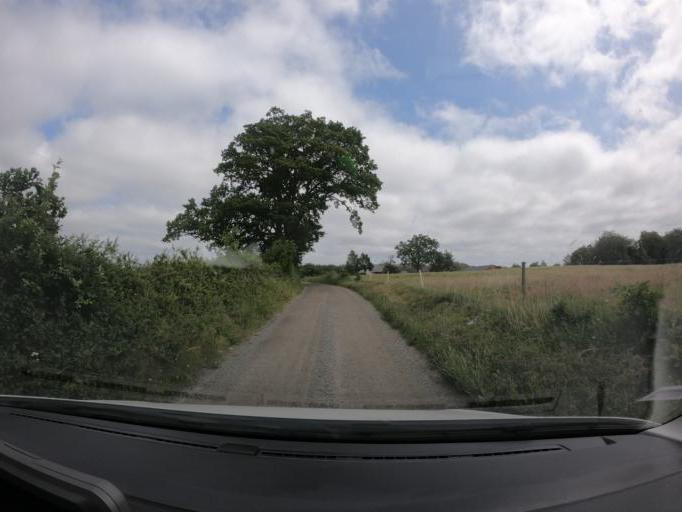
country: SE
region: Skane
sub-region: Hassleholms Kommun
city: Sosdala
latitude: 56.0658
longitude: 13.6641
